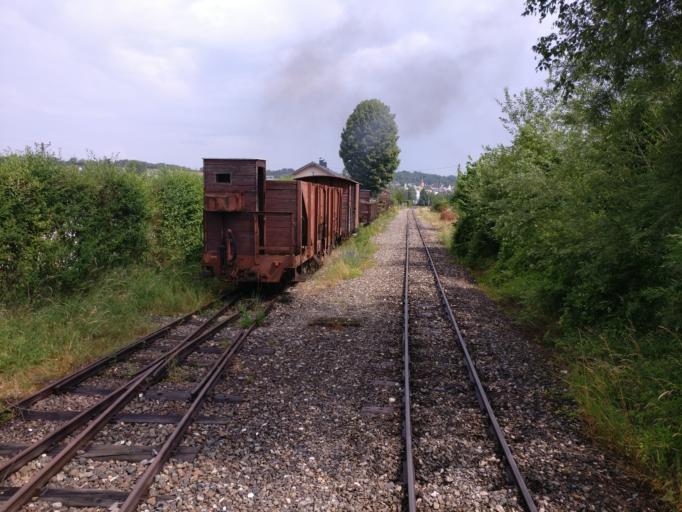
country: AT
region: Upper Austria
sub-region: Politischer Bezirk Steyr-Land
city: Sierning
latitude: 48.0397
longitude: 14.3331
